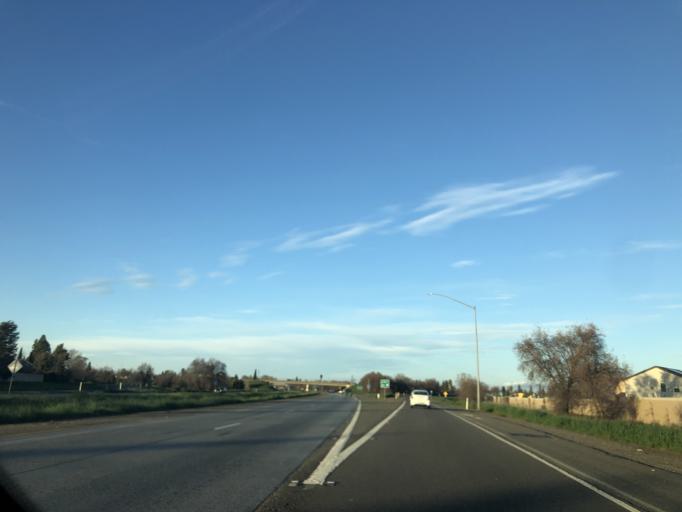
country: US
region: California
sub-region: Yolo County
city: Woodland
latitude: 38.6583
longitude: -121.7524
